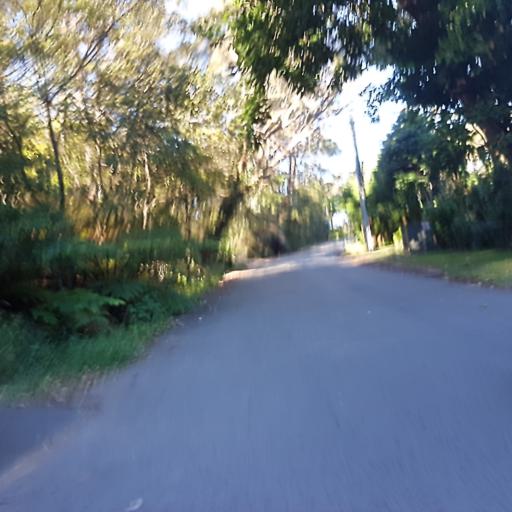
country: AU
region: New South Wales
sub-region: Ku-ring-gai
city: Roseville Chase
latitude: -33.7767
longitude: 151.2035
